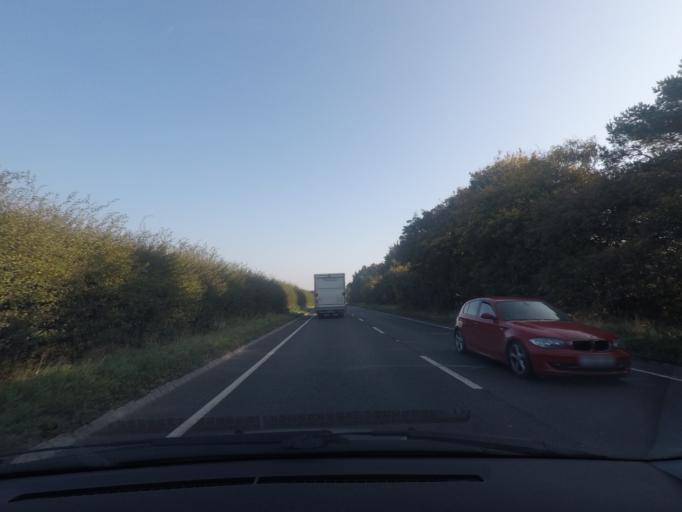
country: GB
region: England
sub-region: City of York
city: Skelton
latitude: 53.9897
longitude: -1.1169
